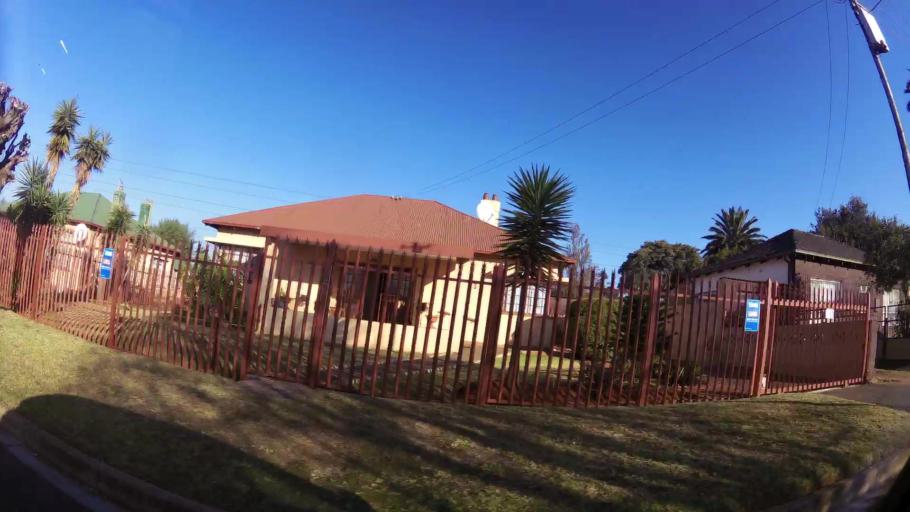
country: ZA
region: Gauteng
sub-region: Ekurhuleni Metropolitan Municipality
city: Germiston
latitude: -26.1955
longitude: 28.1472
